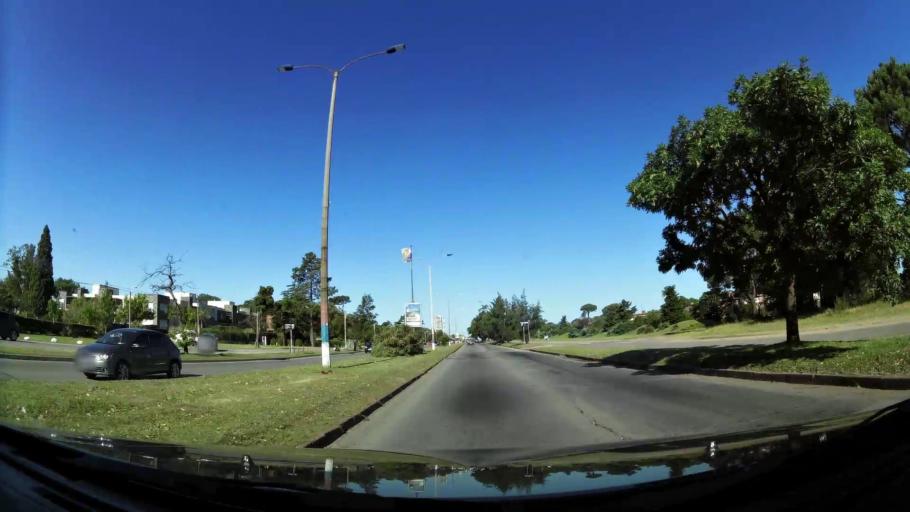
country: UY
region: Canelones
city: Barra de Carrasco
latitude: -34.8761
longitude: -56.0443
